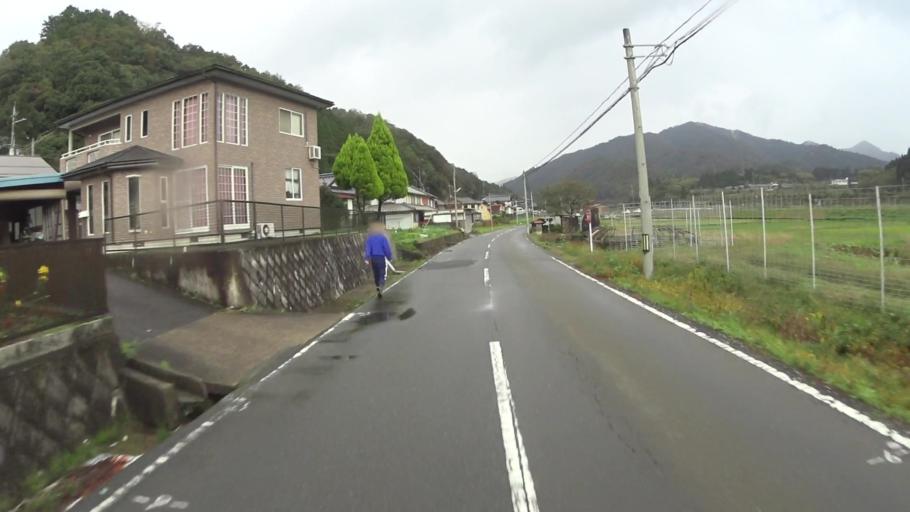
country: JP
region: Kyoto
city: Fukuchiyama
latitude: 35.4141
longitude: 135.1527
